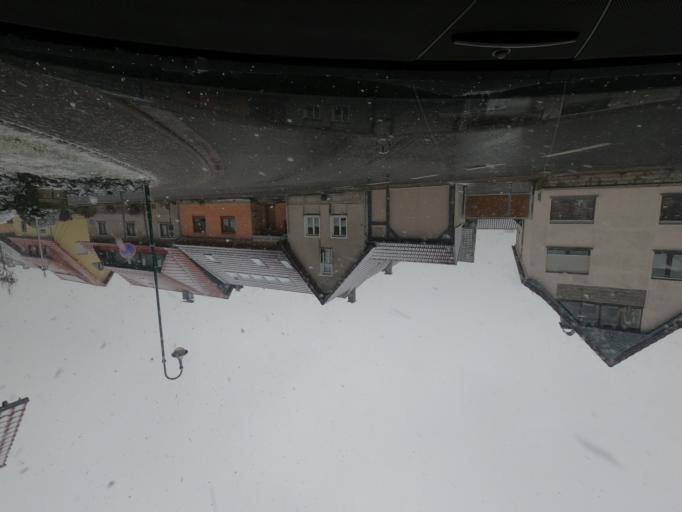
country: DE
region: Thuringia
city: Effelder
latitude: 51.2385
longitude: 10.2495
